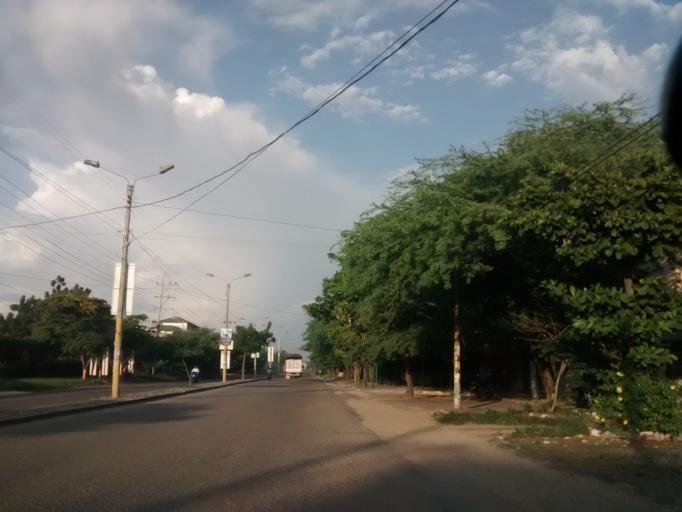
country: CO
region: Tolima
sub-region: Flandes
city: Flandes
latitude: 4.2978
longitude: -74.8211
